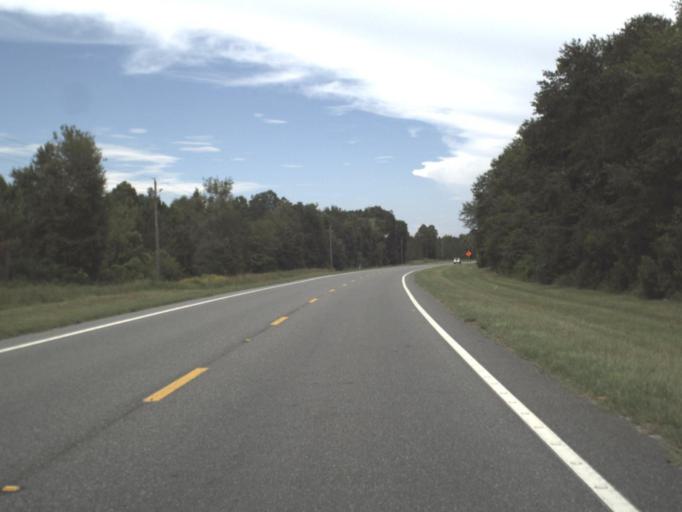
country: US
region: Florida
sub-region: Taylor County
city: Perry
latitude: 30.0968
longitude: -83.4807
